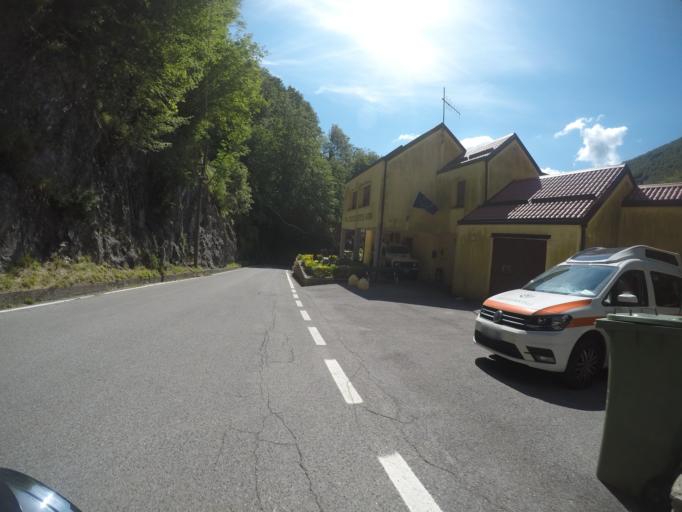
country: IT
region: Tuscany
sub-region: Provincia di Lucca
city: Fontana delle Monache
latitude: 44.0622
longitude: 10.2518
